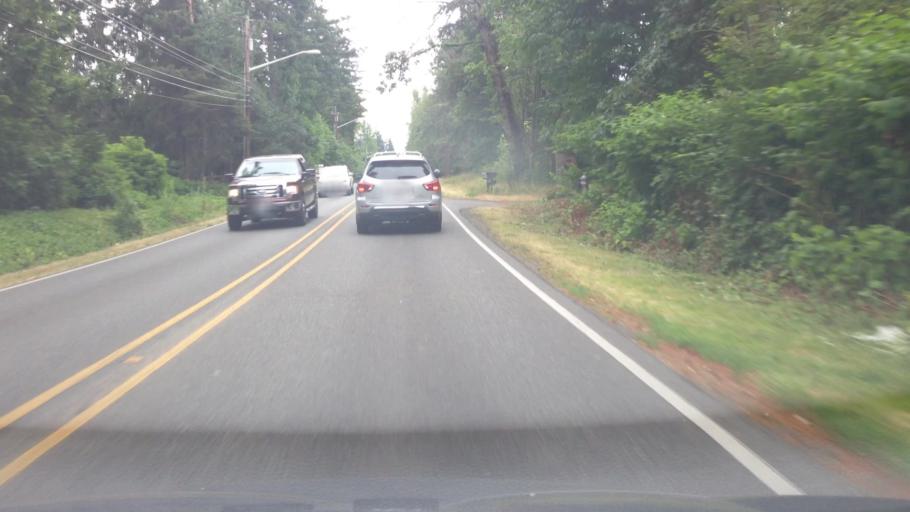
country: US
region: Washington
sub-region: Pierce County
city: South Hill
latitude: 47.1302
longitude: -122.3040
